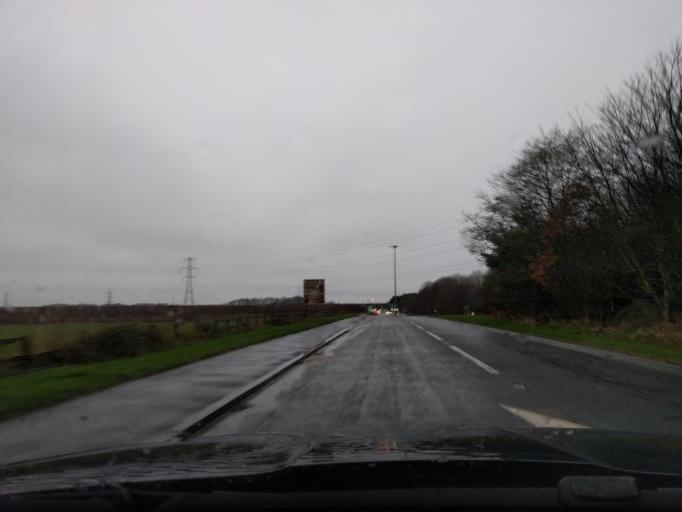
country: GB
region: England
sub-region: Northumberland
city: Lynemouth
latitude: 55.1917
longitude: -1.5361
